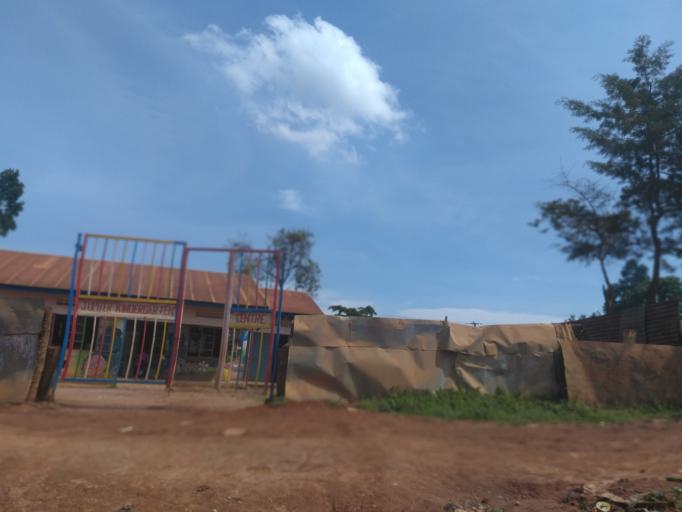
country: UG
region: Central Region
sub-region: Wakiso District
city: Kireka
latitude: 0.4401
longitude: 32.5990
